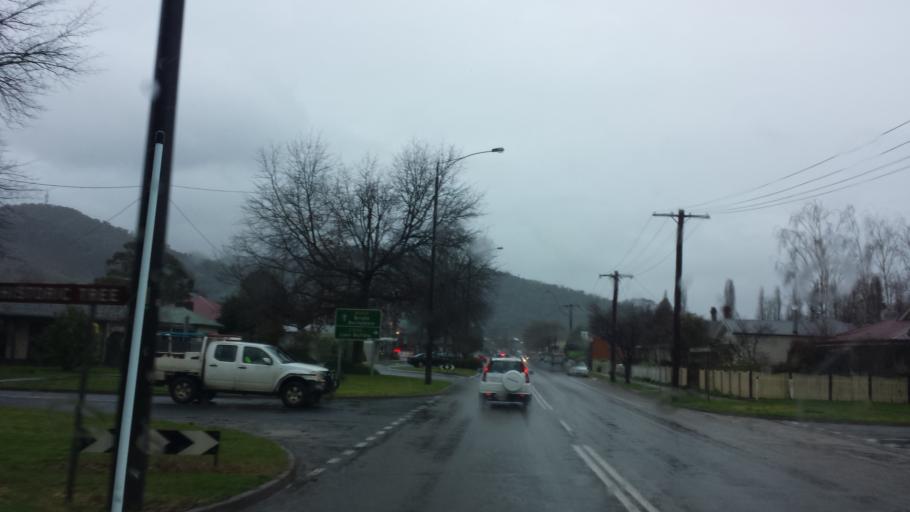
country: AU
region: Victoria
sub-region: Wangaratta
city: Wangaratta
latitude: -36.5594
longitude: 146.7216
